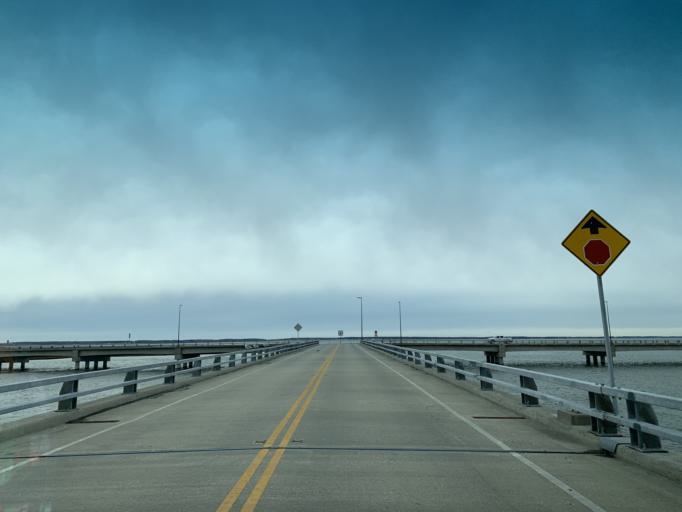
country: US
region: Virginia
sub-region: Accomack County
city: Chincoteague
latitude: 37.9366
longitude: -75.3809
